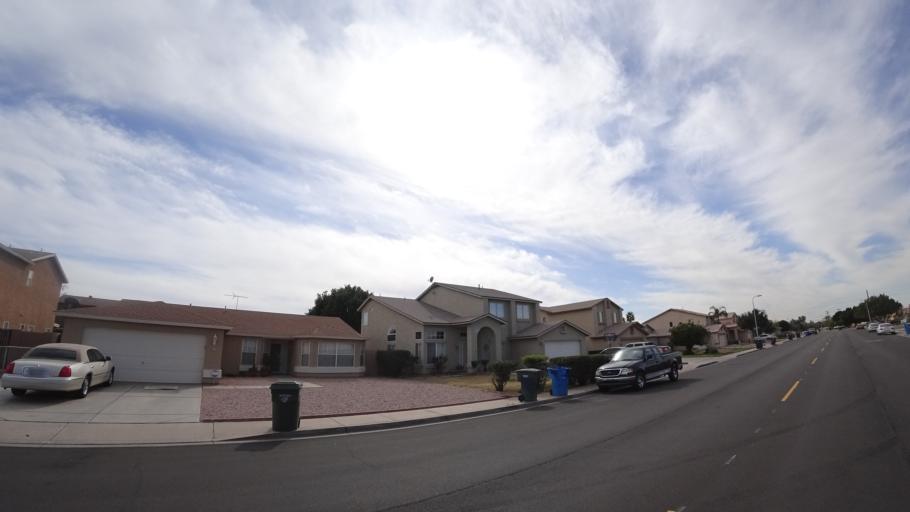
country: US
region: Arizona
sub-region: Maricopa County
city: Tolleson
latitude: 33.4724
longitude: -112.2522
